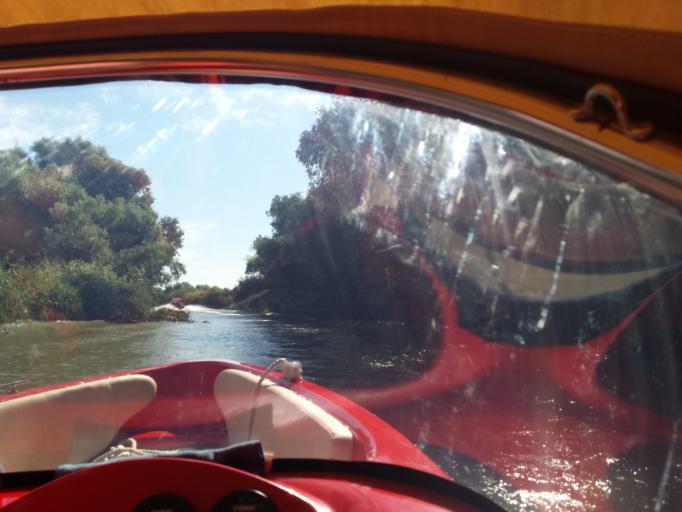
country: RO
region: Tulcea
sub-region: Comuna Pardina
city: Pardina
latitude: 45.2456
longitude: 29.0221
